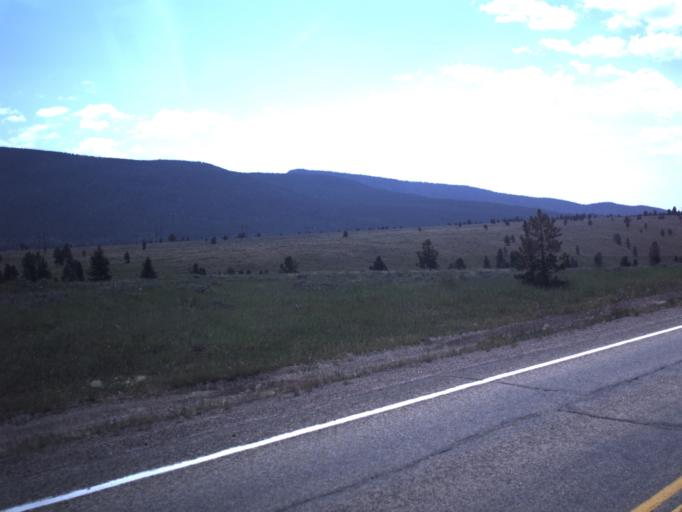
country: US
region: Utah
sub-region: Daggett County
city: Manila
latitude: 40.7965
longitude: -109.4662
